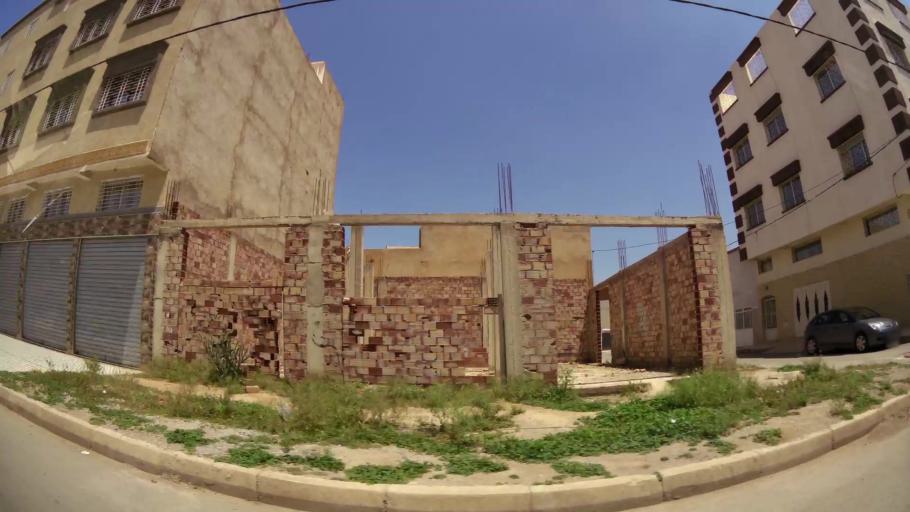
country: MA
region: Oriental
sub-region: Oujda-Angad
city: Oujda
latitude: 34.6888
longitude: -1.8967
